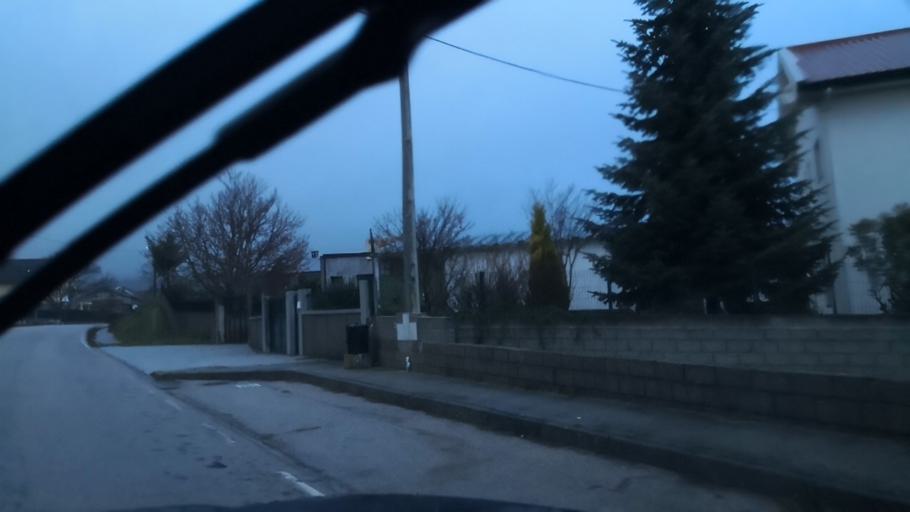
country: PT
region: Vila Real
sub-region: Vila Pouca de Aguiar
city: Vila Pouca de Aguiar
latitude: 41.4550
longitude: -7.5915
